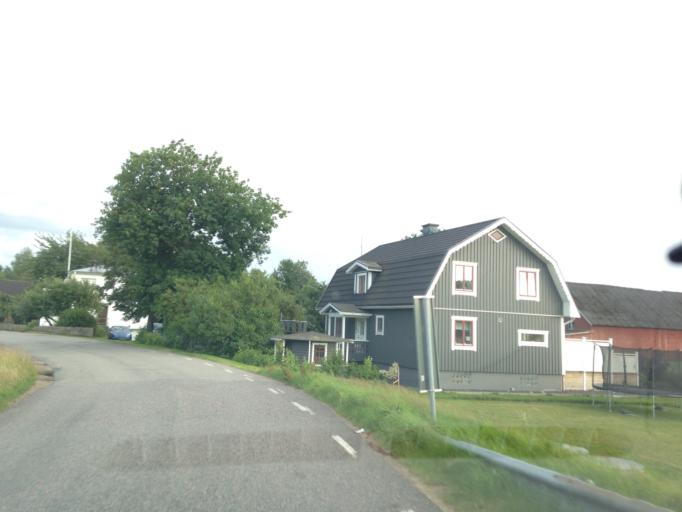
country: SE
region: Halland
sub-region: Varbergs Kommun
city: Tvaaker
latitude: 57.1254
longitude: 12.3906
